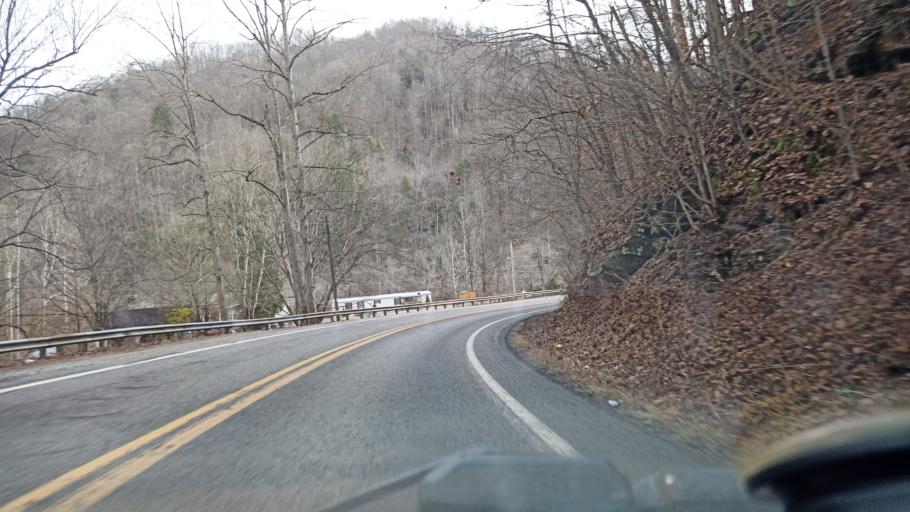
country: US
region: West Virginia
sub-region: Logan County
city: Mallory
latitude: 37.6534
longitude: -81.8519
